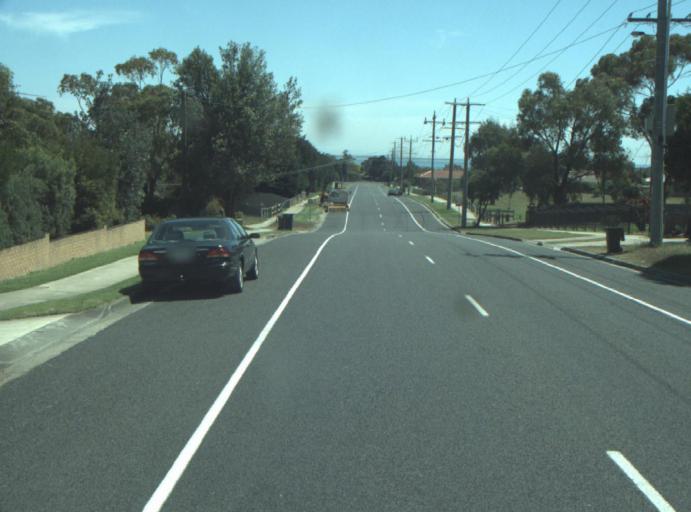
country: AU
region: Victoria
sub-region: Greater Geelong
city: Leopold
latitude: -38.1797
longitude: 144.4663
